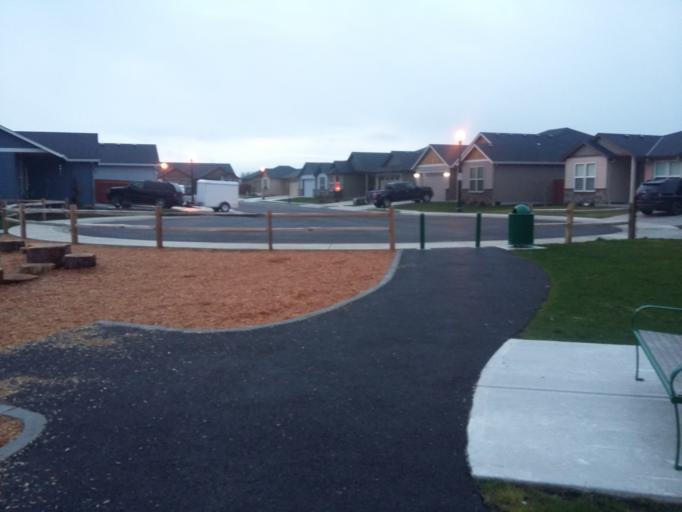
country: US
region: Washington
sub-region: Clark County
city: Battle Ground
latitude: 45.7921
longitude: -122.5585
